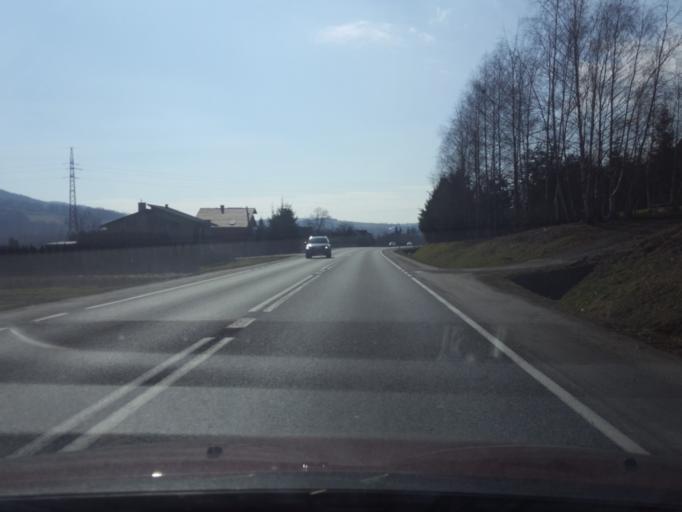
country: PL
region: Lesser Poland Voivodeship
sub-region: Powiat nowosadecki
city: Lososina Dolna
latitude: 49.7626
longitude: 20.6334
